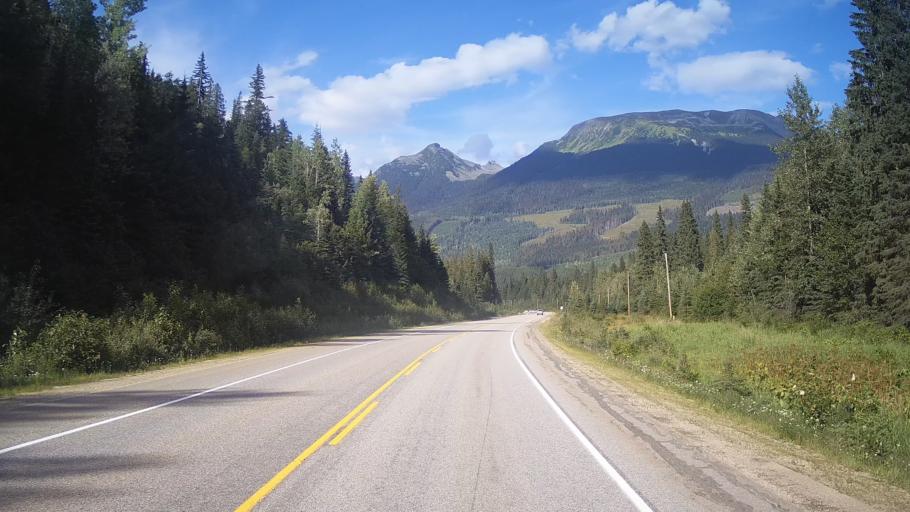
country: CA
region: Alberta
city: Jasper Park Lodge
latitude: 52.5642
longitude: -119.1069
